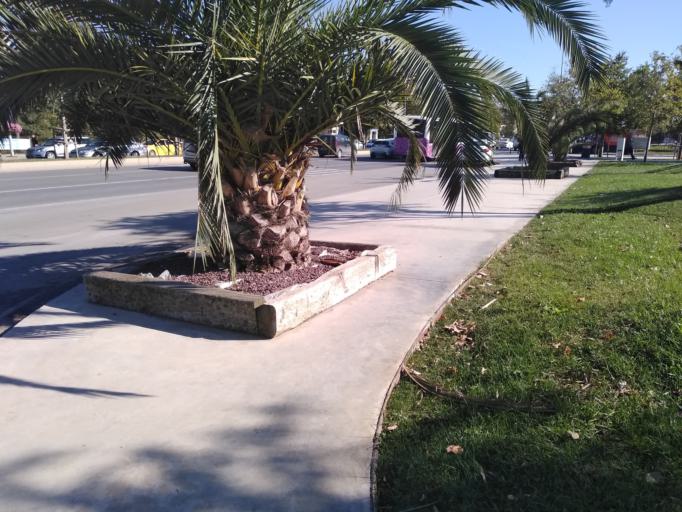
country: TR
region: Istanbul
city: Maltepe
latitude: 40.9201
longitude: 29.1279
